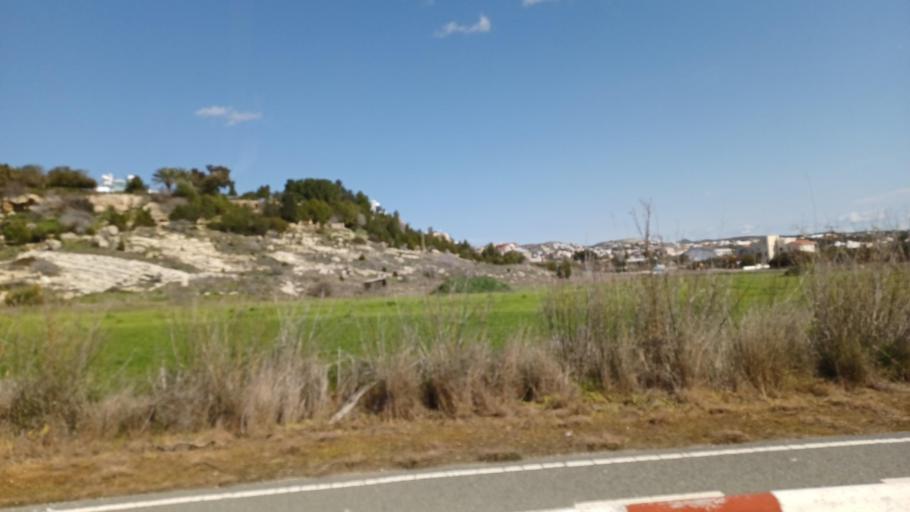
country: CY
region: Pafos
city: Paphos
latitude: 34.7542
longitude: 32.4450
